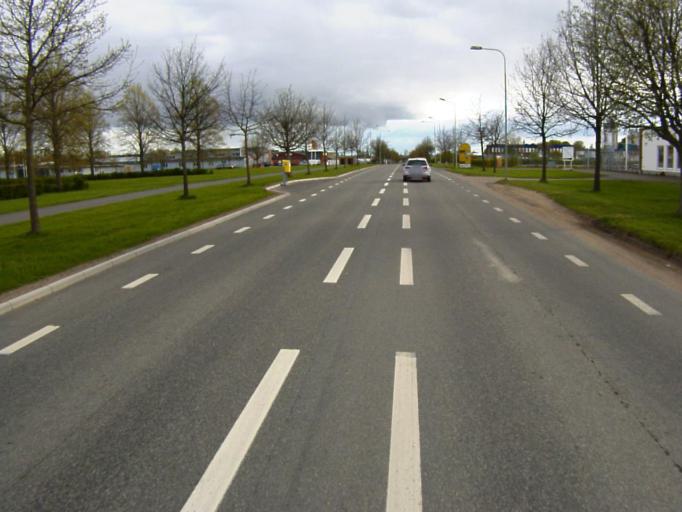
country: SE
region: Skane
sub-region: Kristianstads Kommun
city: Kristianstad
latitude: 56.0503
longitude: 14.1628
